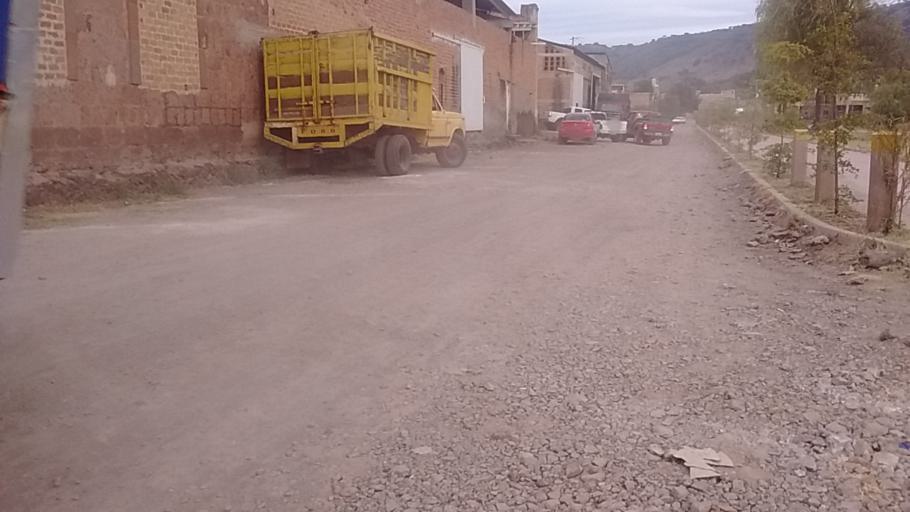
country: MX
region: Jalisco
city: Atotonilco el Alto
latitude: 20.5440
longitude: -102.5149
